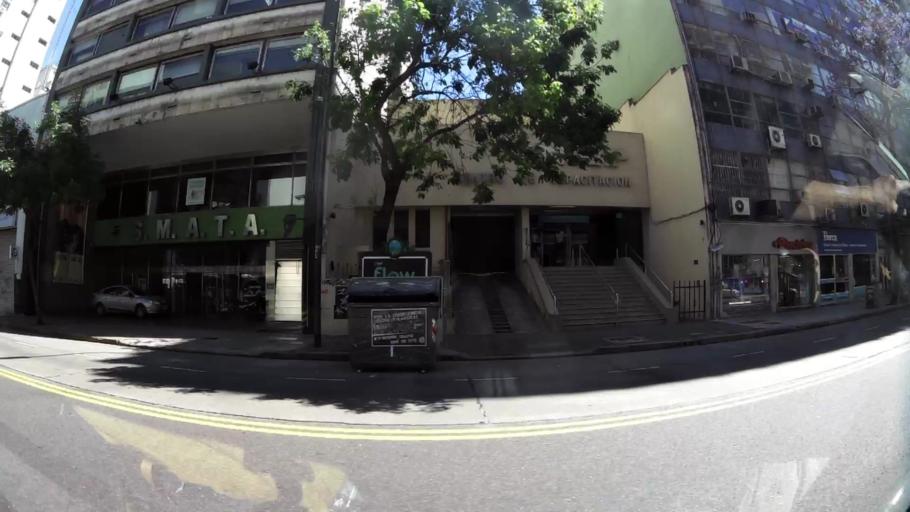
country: AR
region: Buenos Aires F.D.
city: Buenos Aires
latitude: -34.6130
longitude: -58.3751
